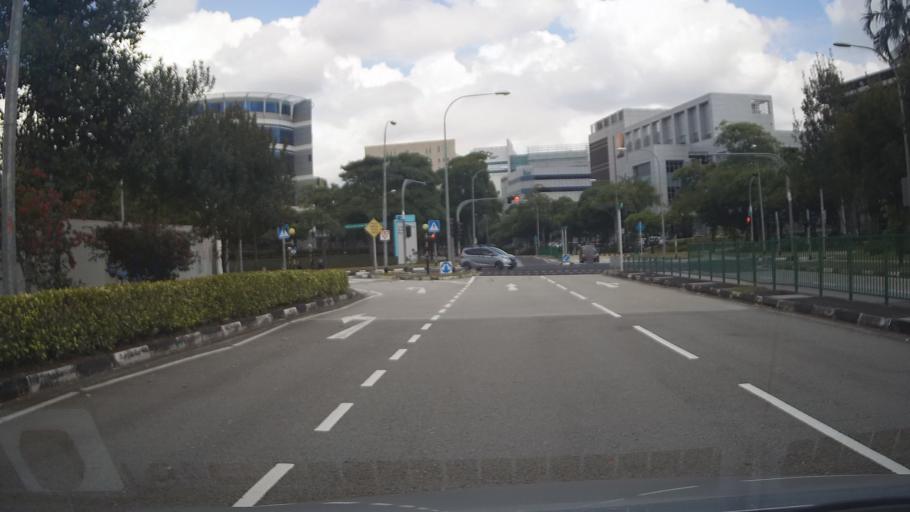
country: SG
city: Singapore
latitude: 1.3230
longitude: 103.7504
